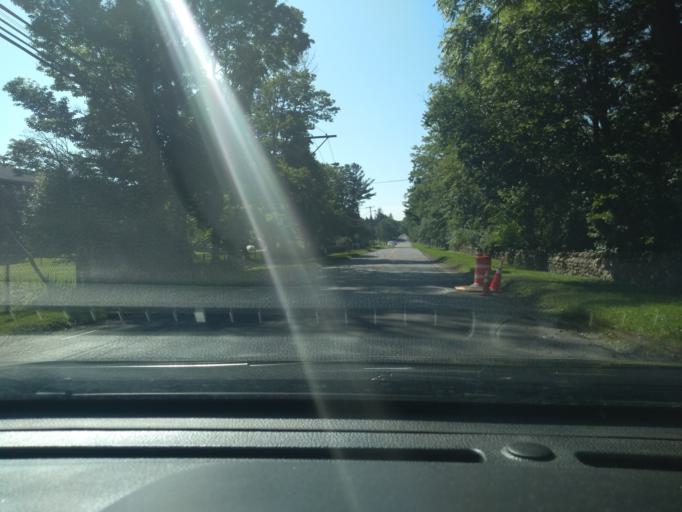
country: US
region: New York
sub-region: Erie County
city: Billington Heights
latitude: 42.7737
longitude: -78.6360
